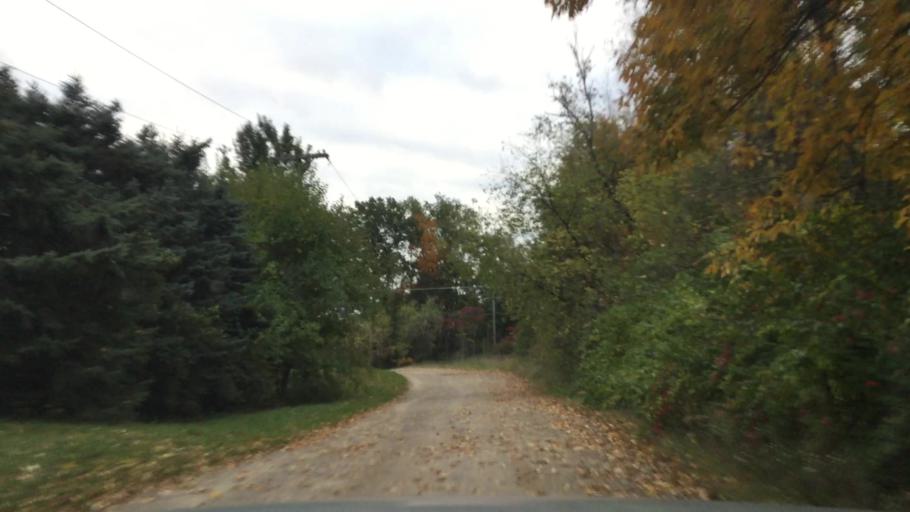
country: US
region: Michigan
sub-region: Genesee County
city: Fenton
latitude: 42.6789
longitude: -83.7389
